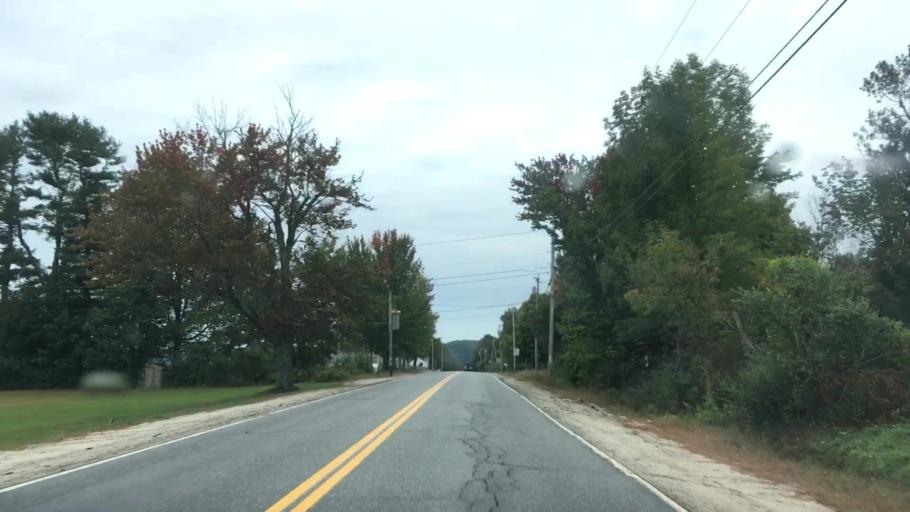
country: US
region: Maine
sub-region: Cumberland County
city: Raymond
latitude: 43.9381
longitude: -70.4478
